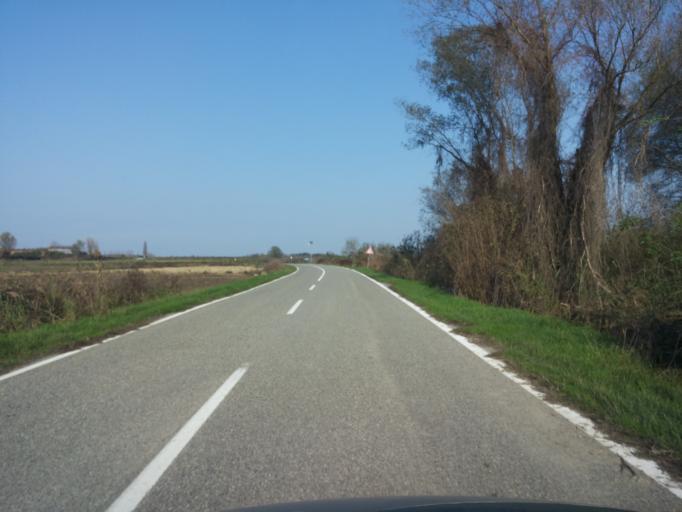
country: IT
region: Piedmont
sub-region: Provincia di Vercelli
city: Caresana
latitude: 45.2272
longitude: 8.4960
